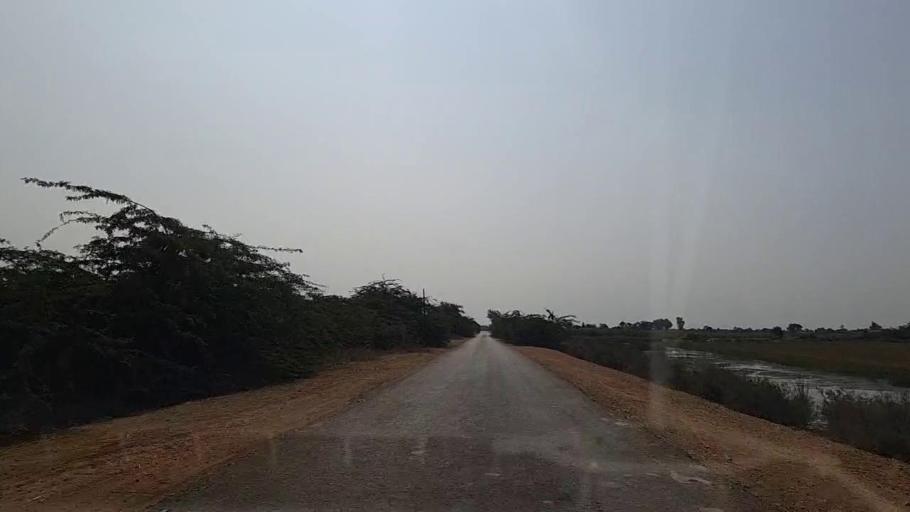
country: PK
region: Sindh
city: Chuhar Jamali
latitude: 24.3144
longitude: 67.9397
